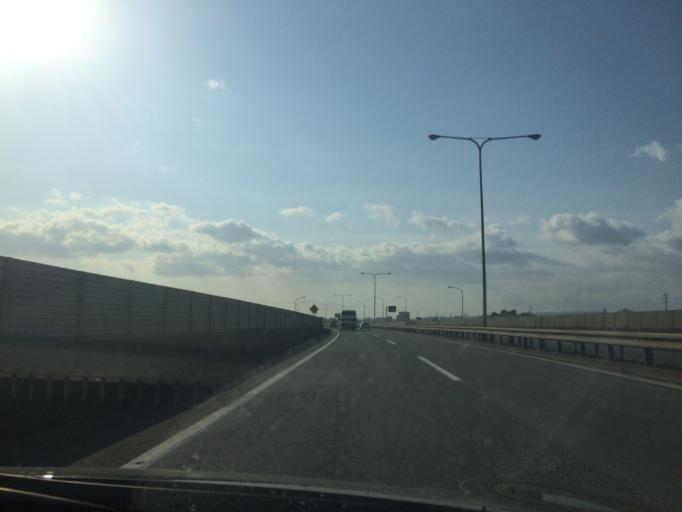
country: JP
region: Hokkaido
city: Sapporo
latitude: 43.0598
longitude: 141.4251
